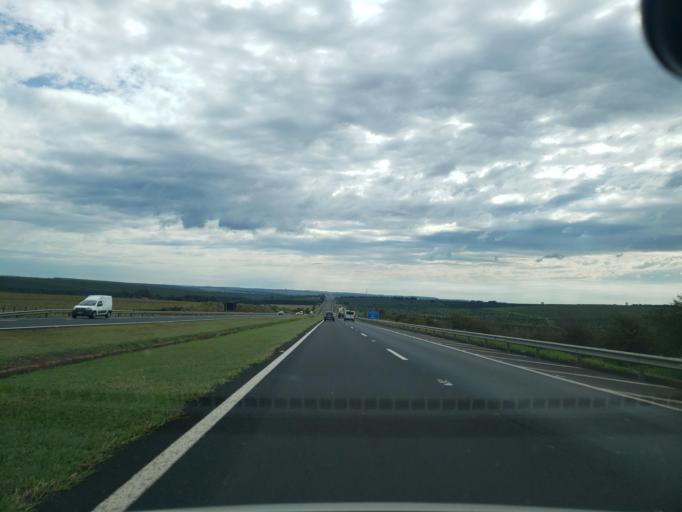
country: BR
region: Sao Paulo
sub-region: Bauru
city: Bauru
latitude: -22.1850
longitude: -49.2149
